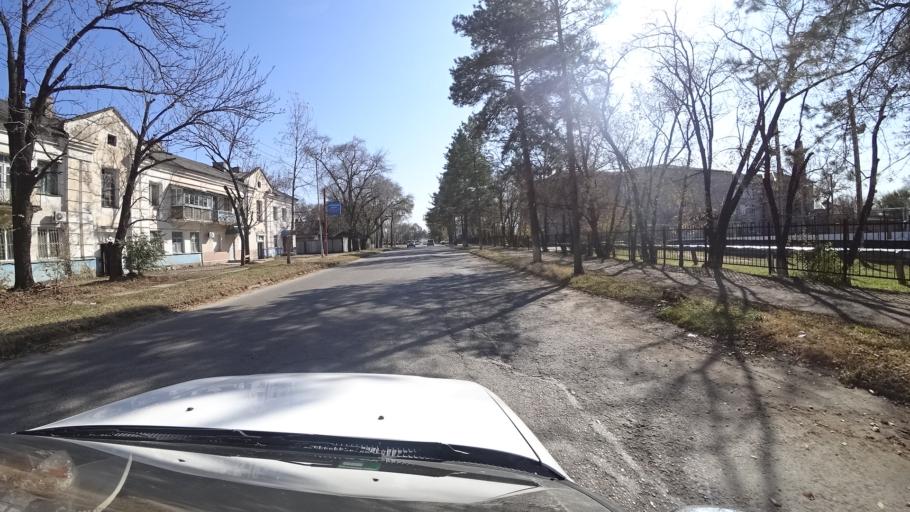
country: RU
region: Primorskiy
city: Dal'nerechensk
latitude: 45.9288
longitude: 133.7326
